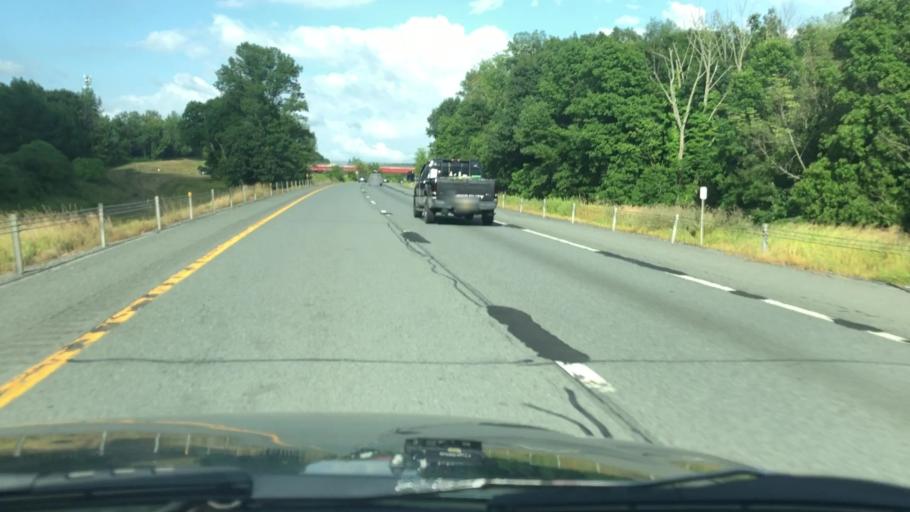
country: US
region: New York
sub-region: Orange County
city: Otisville
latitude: 41.4060
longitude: -74.5049
